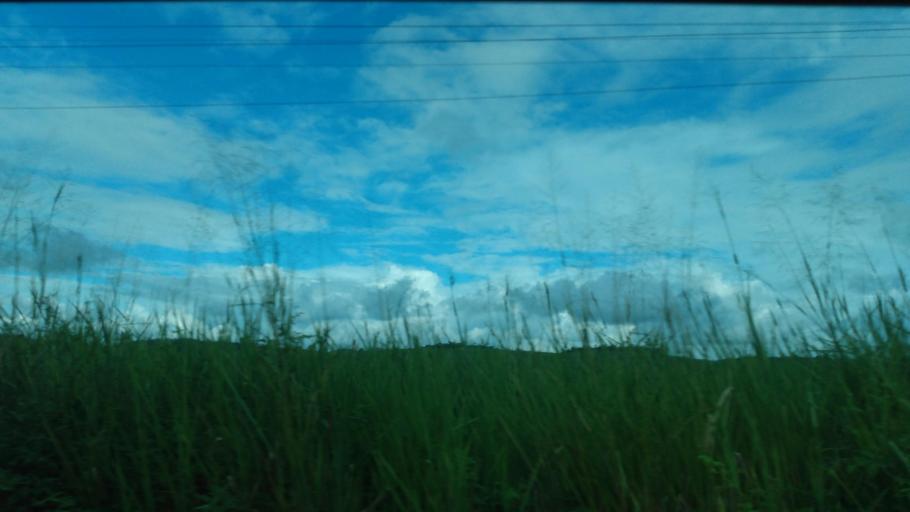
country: BR
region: Pernambuco
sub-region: Catende
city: Catende
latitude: -8.6985
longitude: -35.7369
